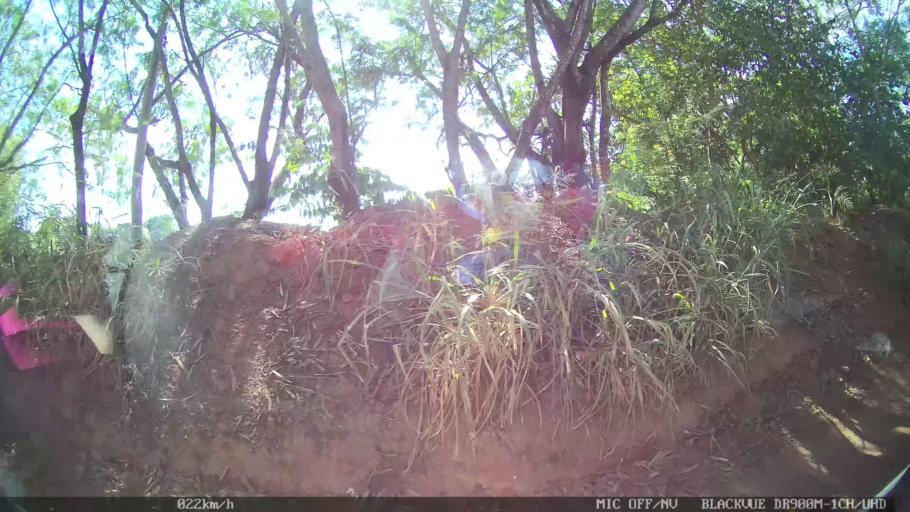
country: BR
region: Sao Paulo
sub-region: Hortolandia
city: Hortolandia
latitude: -22.8780
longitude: -47.2613
